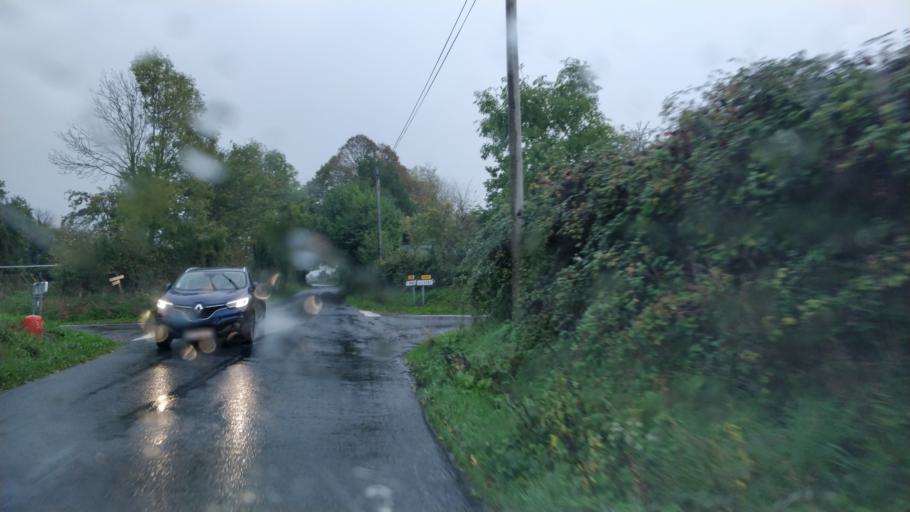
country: FR
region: Lower Normandy
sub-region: Departement de la Manche
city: Brehal
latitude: 48.9016
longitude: -1.5299
